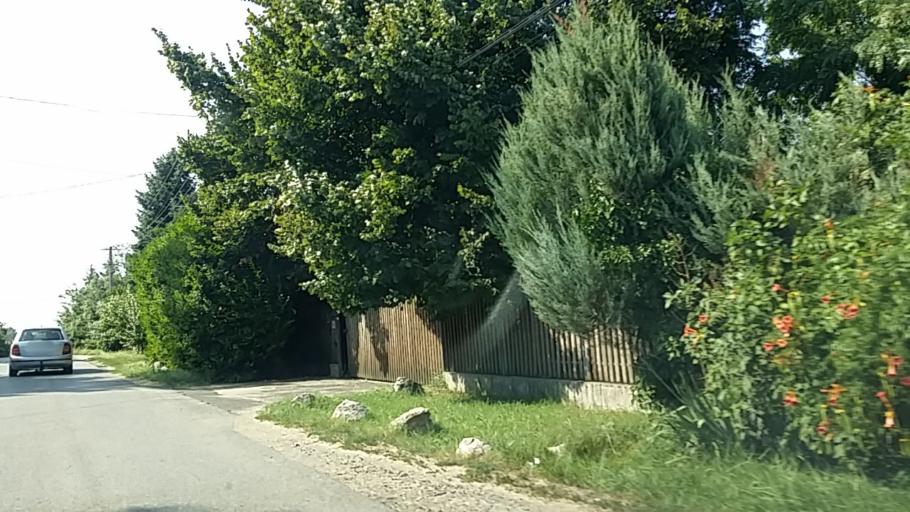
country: HU
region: Pest
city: Erdokertes
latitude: 47.6677
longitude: 19.3328
